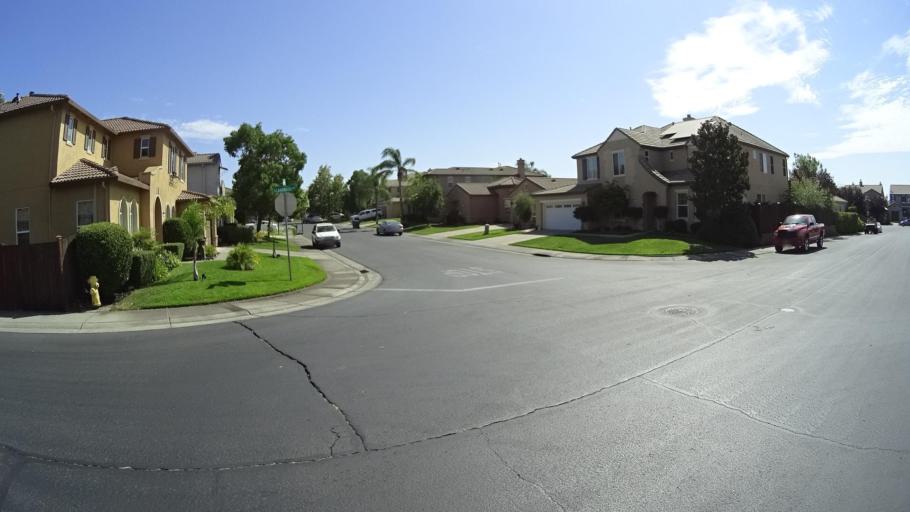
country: US
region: California
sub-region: Placer County
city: Roseville
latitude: 38.8050
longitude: -121.2881
